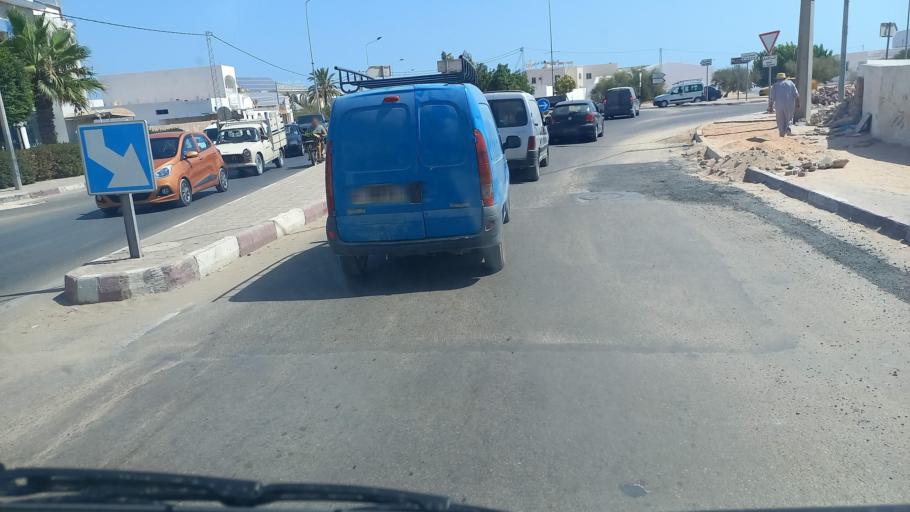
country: TN
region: Madanin
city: Houmt Souk
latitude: 33.8682
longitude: 10.8682
